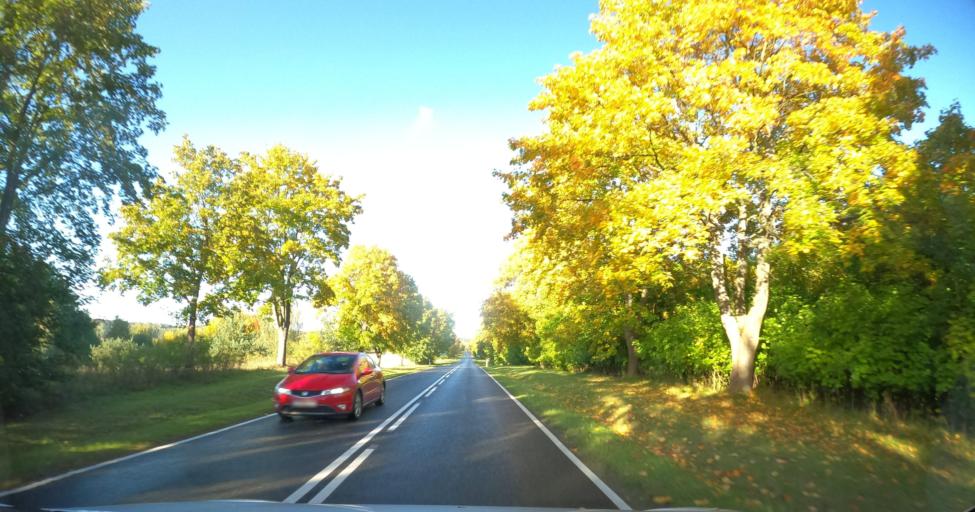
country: PL
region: Lubusz
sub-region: Powiat zielonogorski
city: Zabor
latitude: 51.9390
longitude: 15.6648
